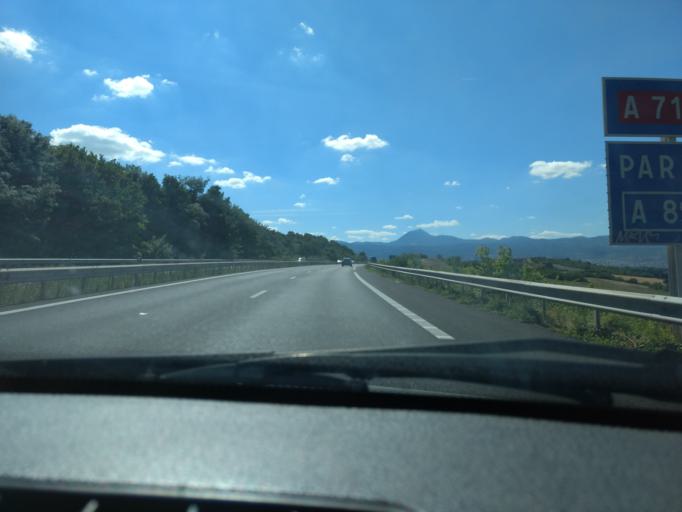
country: FR
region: Auvergne
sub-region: Departement du Puy-de-Dome
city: Aulnat
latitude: 45.7731
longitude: 3.1684
